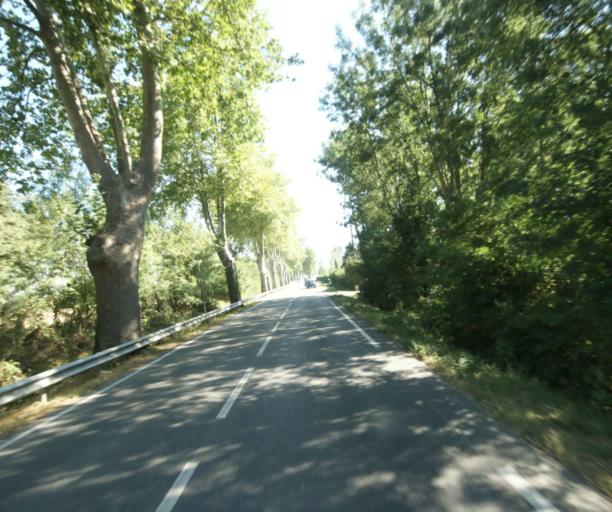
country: FR
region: Midi-Pyrenees
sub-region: Departement de la Haute-Garonne
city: Revel
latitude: 43.4716
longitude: 2.0131
